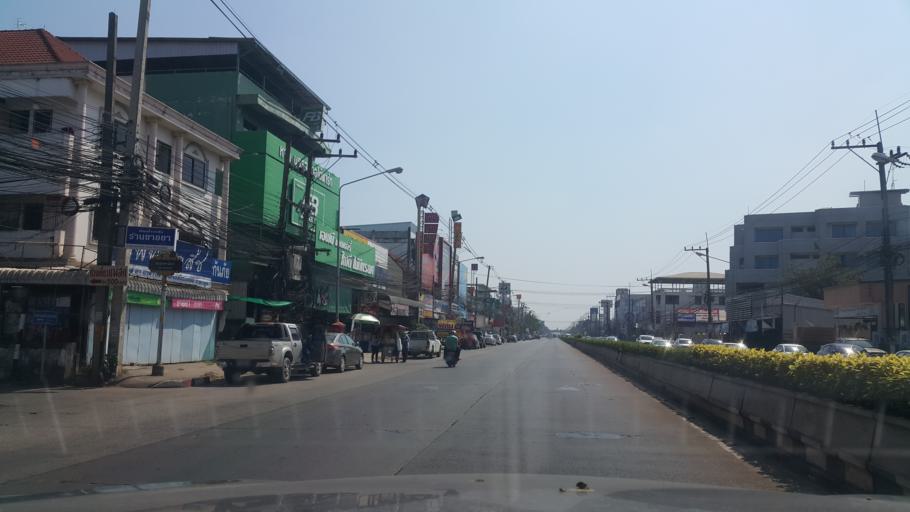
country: TH
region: Changwat Udon Thani
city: Udon Thani
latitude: 17.3933
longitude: 102.7986
